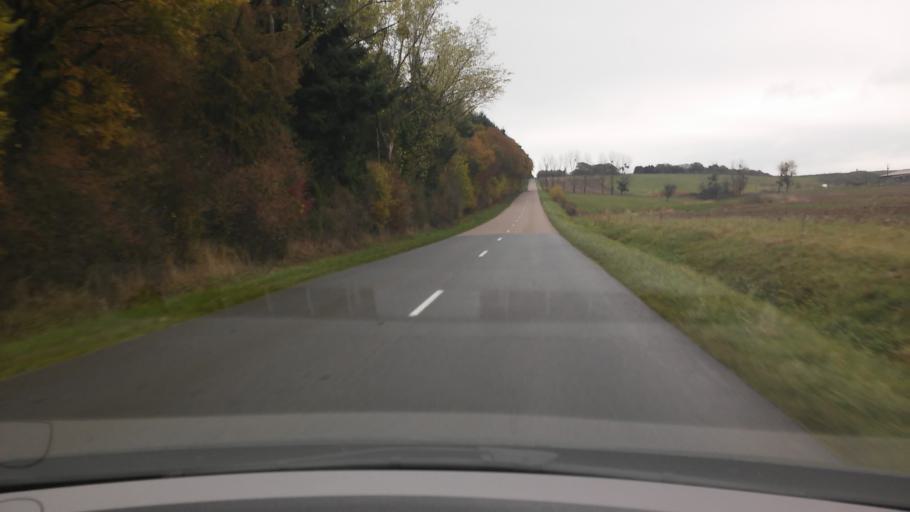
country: FR
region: Lorraine
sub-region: Departement de la Moselle
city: Rurange-les-Thionville
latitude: 49.2818
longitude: 6.2493
